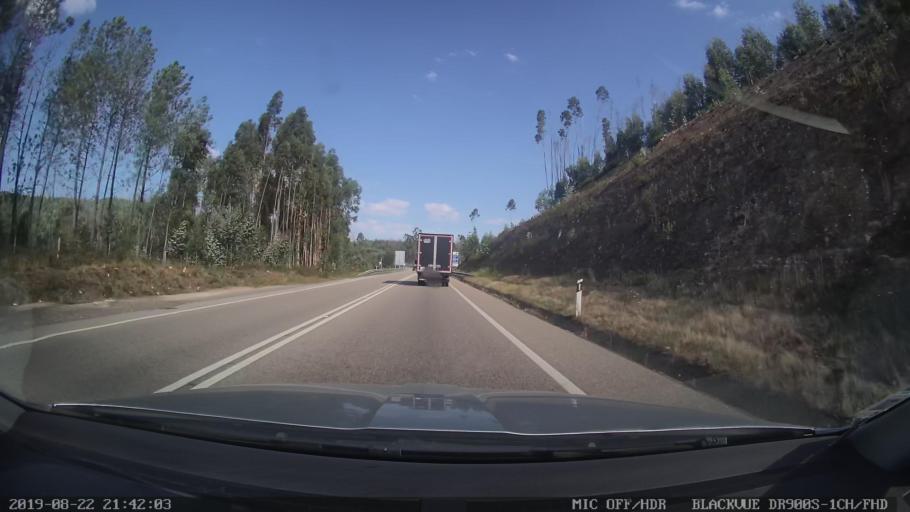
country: PT
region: Leiria
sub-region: Figueiro Dos Vinhos
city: Figueiro dos Vinhos
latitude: 39.9295
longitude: -8.3350
